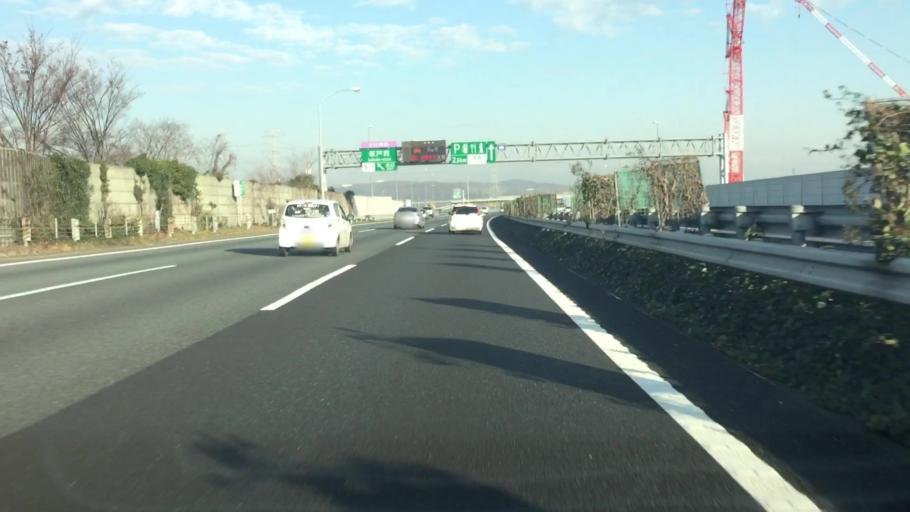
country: JP
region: Saitama
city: Sakado
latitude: 35.9623
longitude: 139.3807
